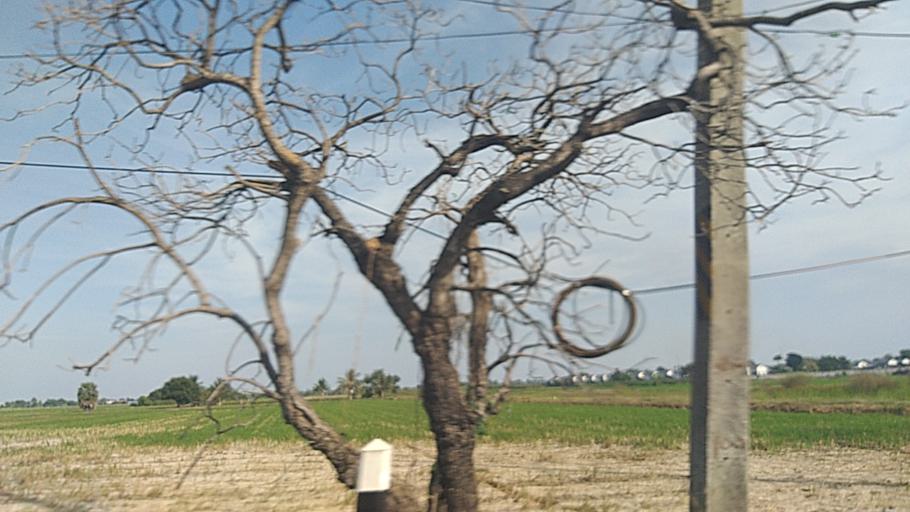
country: TH
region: Pathum Thani
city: Lam Luk Ka
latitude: 13.9482
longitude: 100.7126
